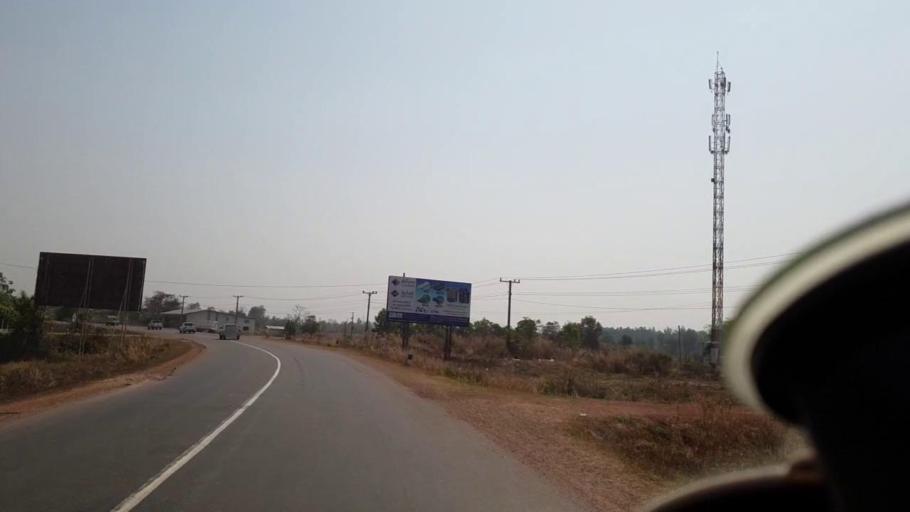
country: TH
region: Nong Khai
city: Phon Phisai
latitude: 18.0467
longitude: 102.8805
